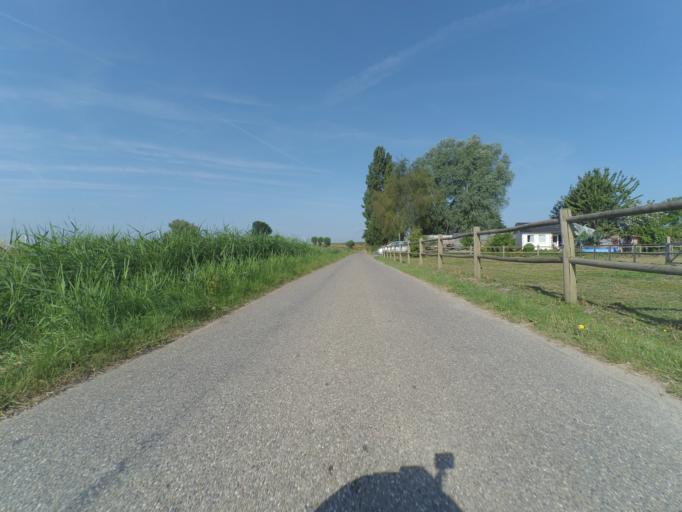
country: NL
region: North Brabant
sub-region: Gemeente Woensdrecht
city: Woensdrecht
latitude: 51.4261
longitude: 4.2546
